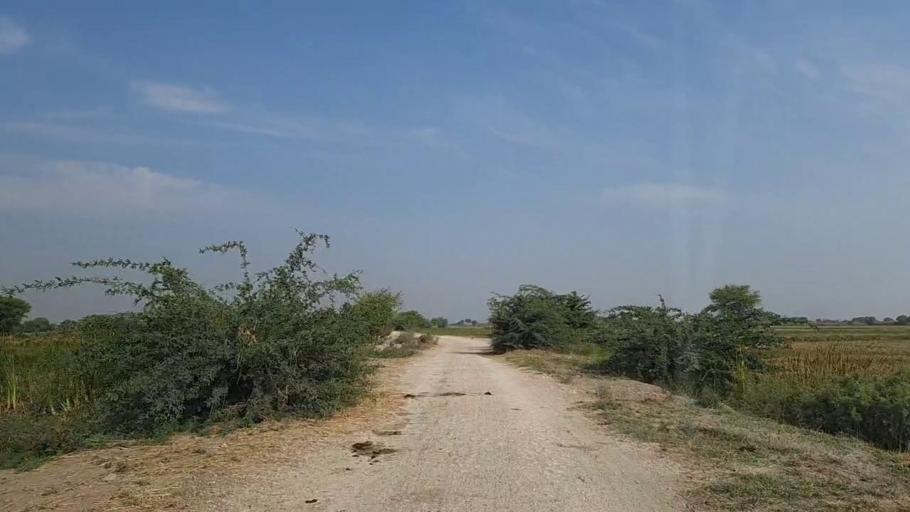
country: PK
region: Sindh
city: Mirpur Batoro
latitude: 24.7133
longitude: 68.2231
